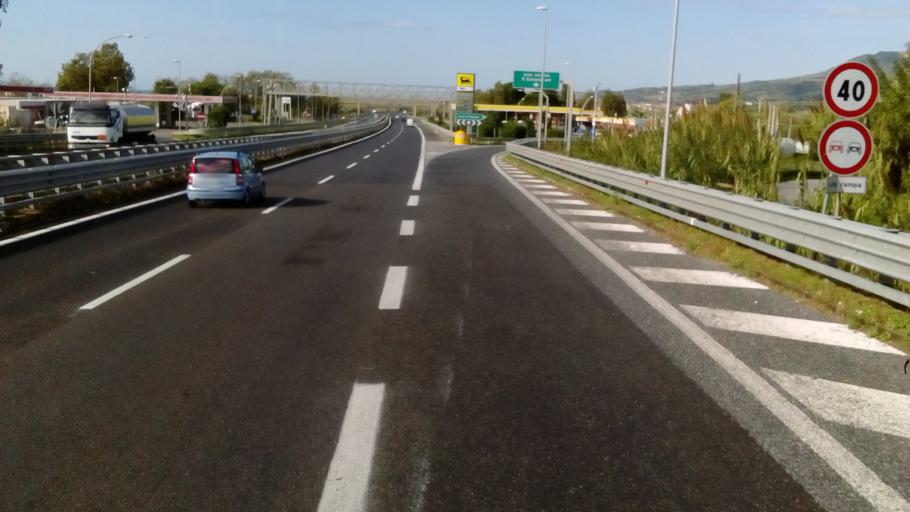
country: IT
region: Calabria
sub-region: Provincia di Catanzaro
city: Santa Eufemia Lamezia
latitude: 38.9293
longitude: 16.2392
